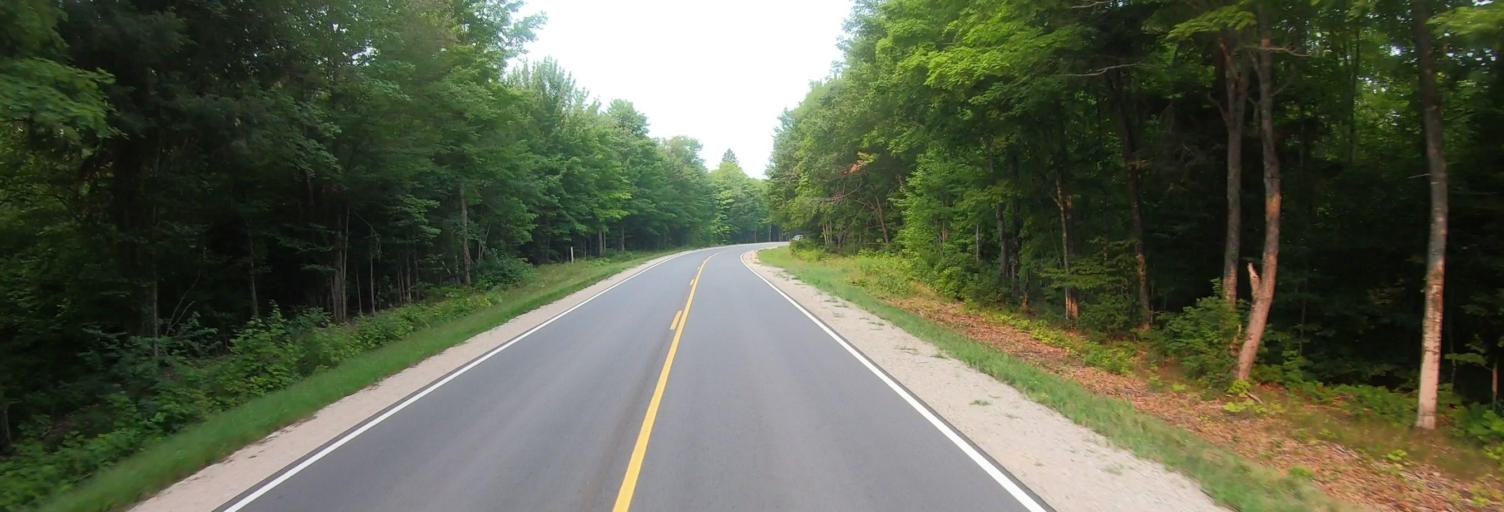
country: US
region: Michigan
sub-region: Luce County
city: Newberry
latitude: 46.4852
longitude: -85.0927
